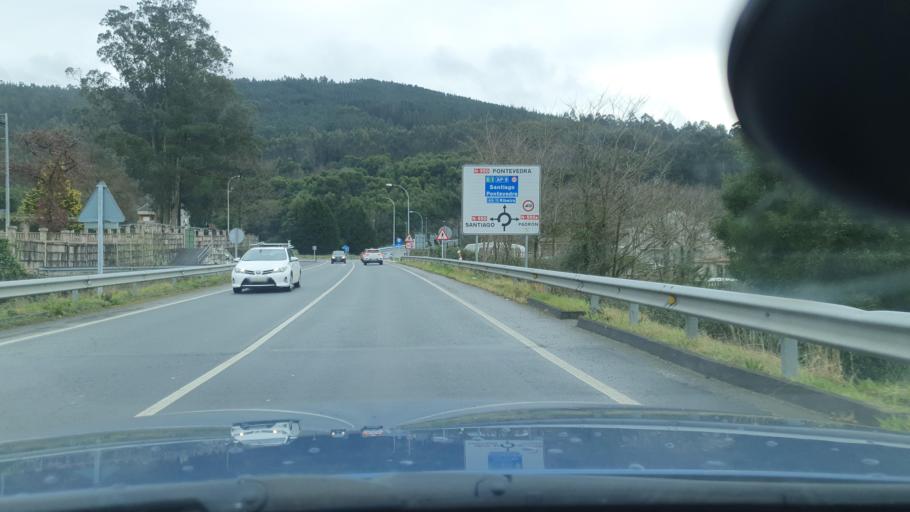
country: ES
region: Galicia
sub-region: Provincia da Coruna
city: Padron
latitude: 42.7562
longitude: -8.6539
